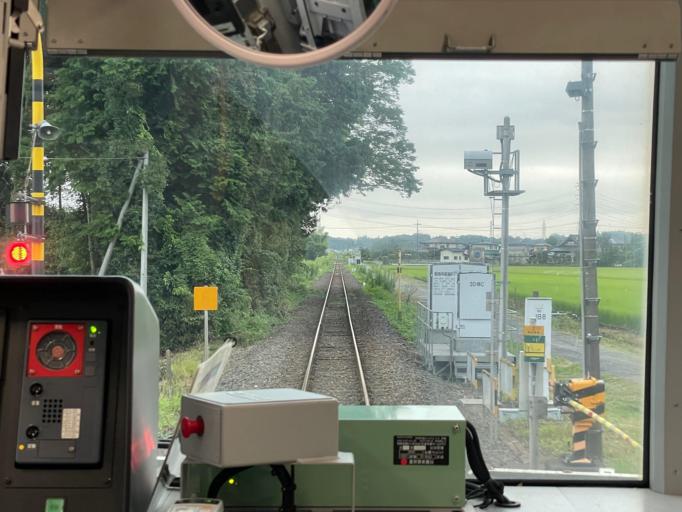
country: JP
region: Tochigi
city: Ujiie
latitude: 36.6496
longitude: 140.0076
